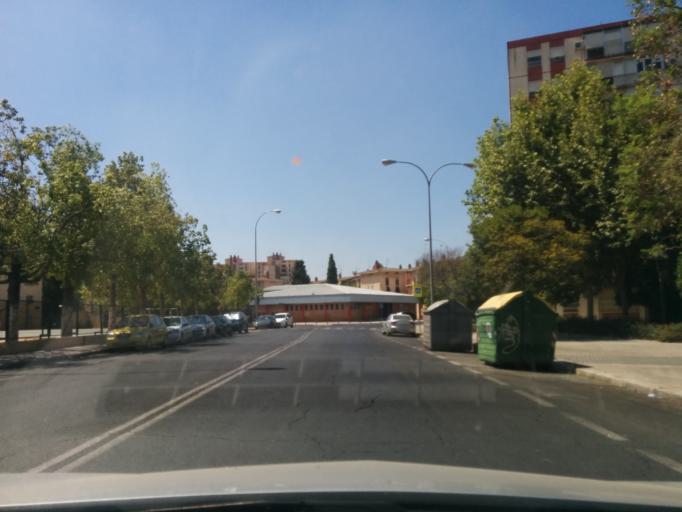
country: ES
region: Andalusia
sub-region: Provincia de Sevilla
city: Sevilla
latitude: 37.3633
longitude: -5.9692
